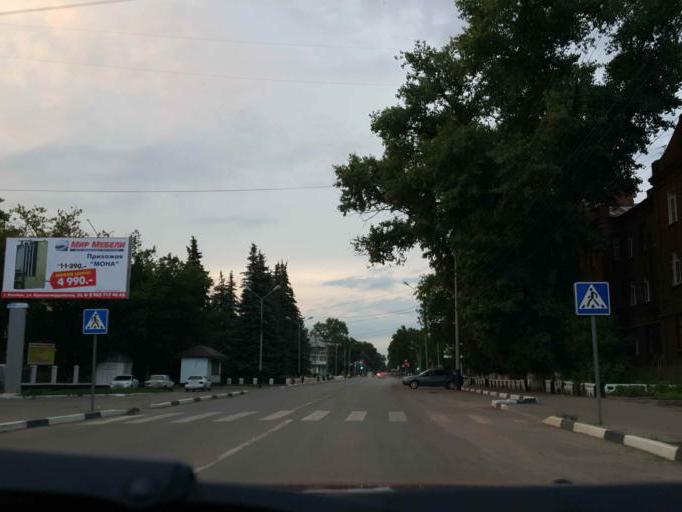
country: RU
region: Tambov
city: Kotovsk
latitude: 52.5856
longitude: 41.4977
